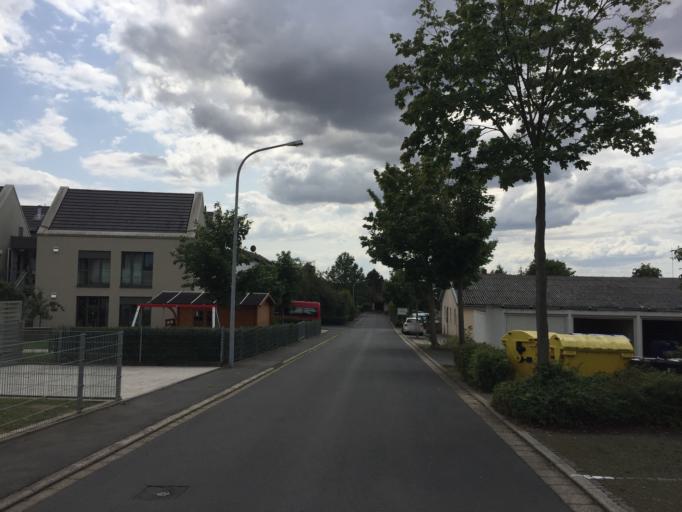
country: DE
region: Hesse
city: Schwalmstadt
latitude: 50.9191
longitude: 9.2321
